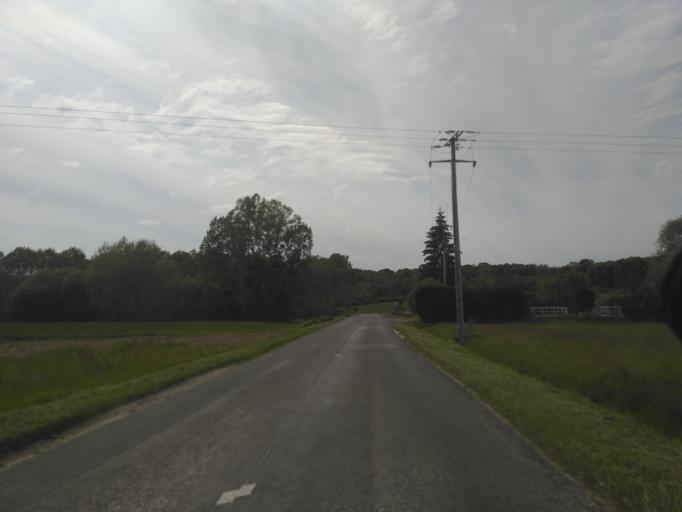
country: FR
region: Ile-de-France
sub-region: Departement de Seine-et-Marne
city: Chaumes-en-Brie
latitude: 48.6662
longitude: 2.8233
